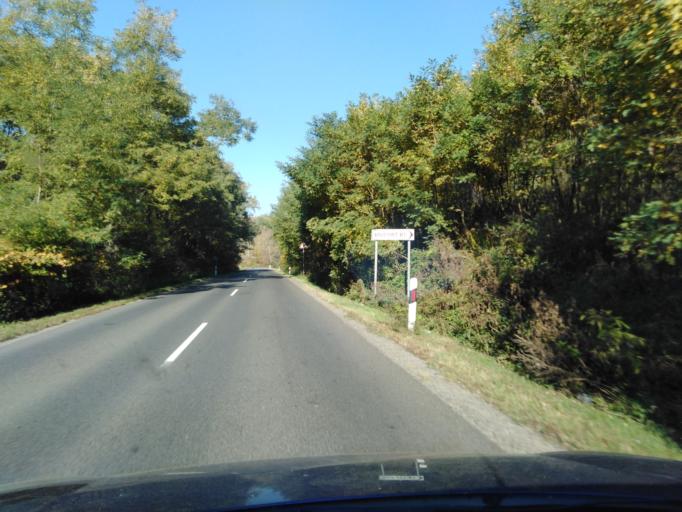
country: HU
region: Nograd
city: Salgotarjan
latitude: 48.1229
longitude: 19.7779
